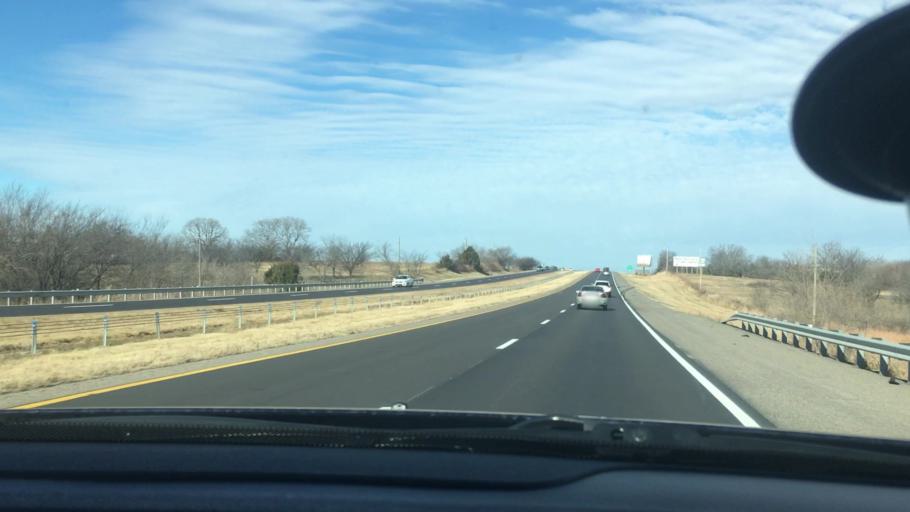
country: US
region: Oklahoma
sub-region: Cleveland County
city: Noble
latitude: 35.1032
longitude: -97.4303
